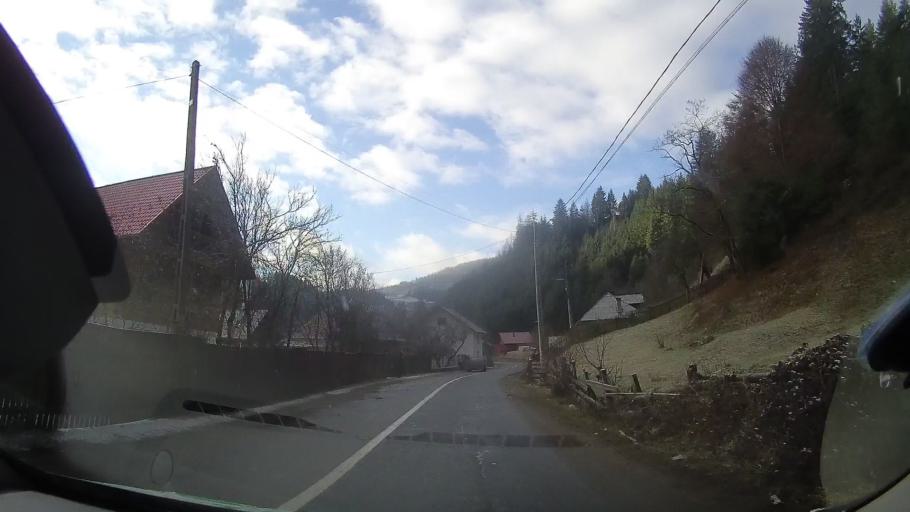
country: RO
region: Alba
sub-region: Comuna Albac
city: Albac
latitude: 46.4535
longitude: 22.9723
